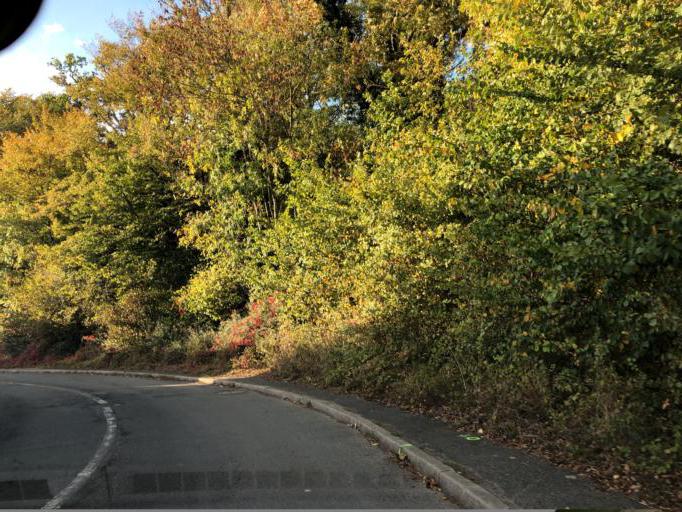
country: FR
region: Ile-de-France
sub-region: Departement des Hauts-de-Seine
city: Chaville
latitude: 48.7997
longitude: 2.1970
